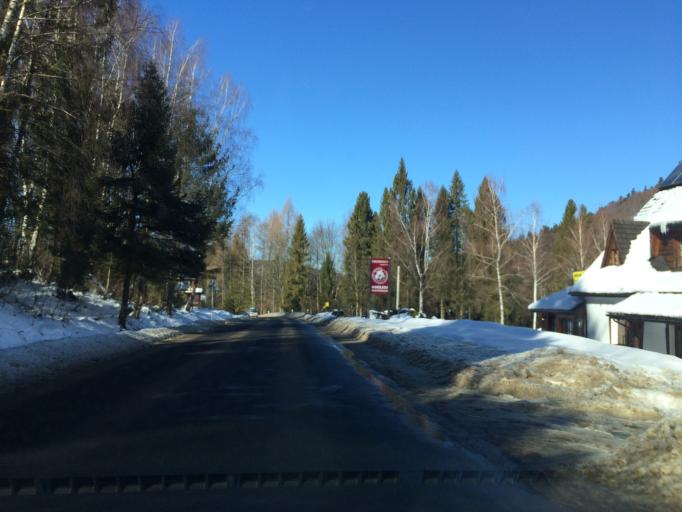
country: PL
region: Subcarpathian Voivodeship
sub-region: Powiat leski
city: Cisna
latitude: 49.1896
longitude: 22.3822
